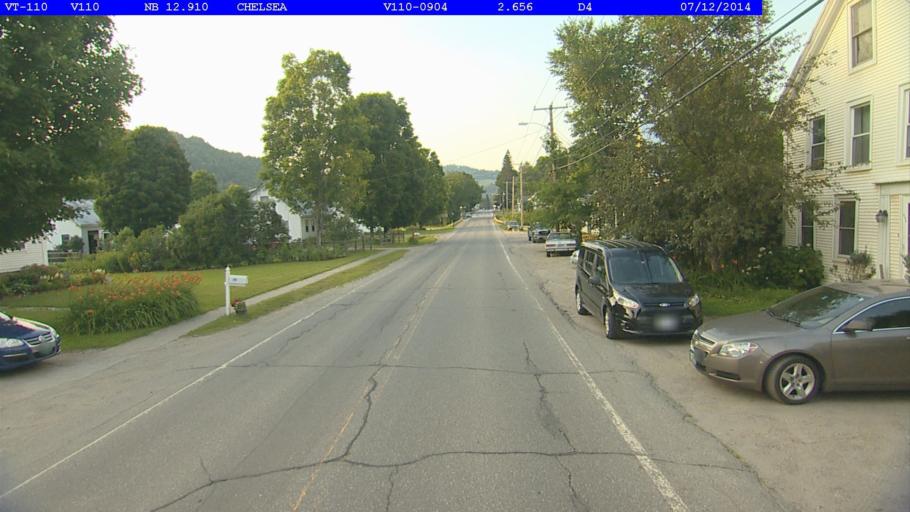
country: US
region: Vermont
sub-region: Orange County
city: Chelsea
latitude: 43.9847
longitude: -72.4483
